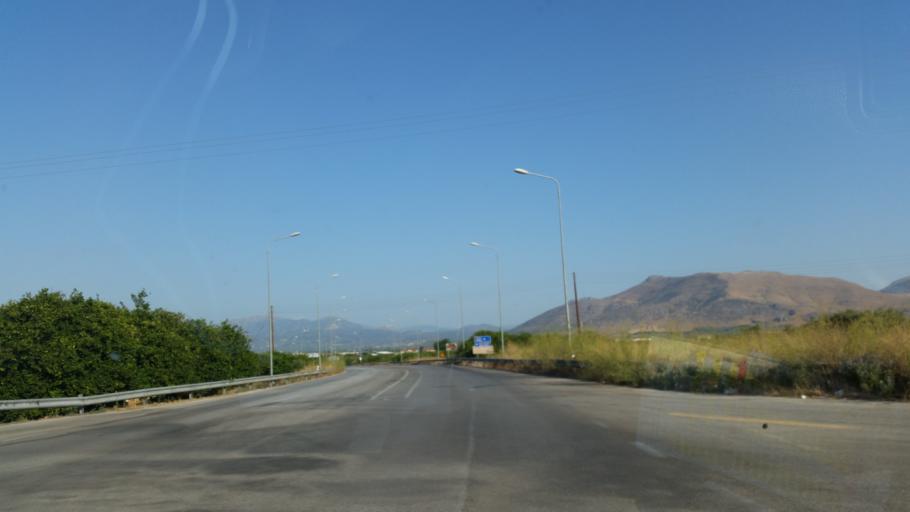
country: GR
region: Peloponnese
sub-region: Nomos Argolidos
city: Ayia Trias
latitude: 37.6405
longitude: 22.8156
